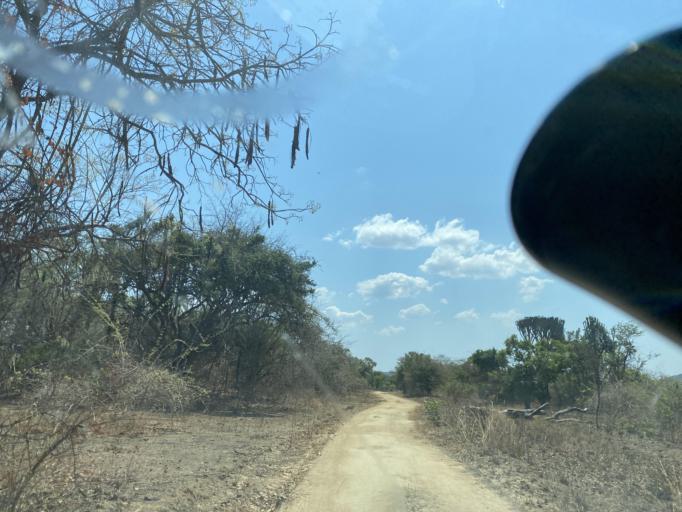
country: ZM
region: Lusaka
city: Chongwe
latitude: -15.0810
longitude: 29.5158
